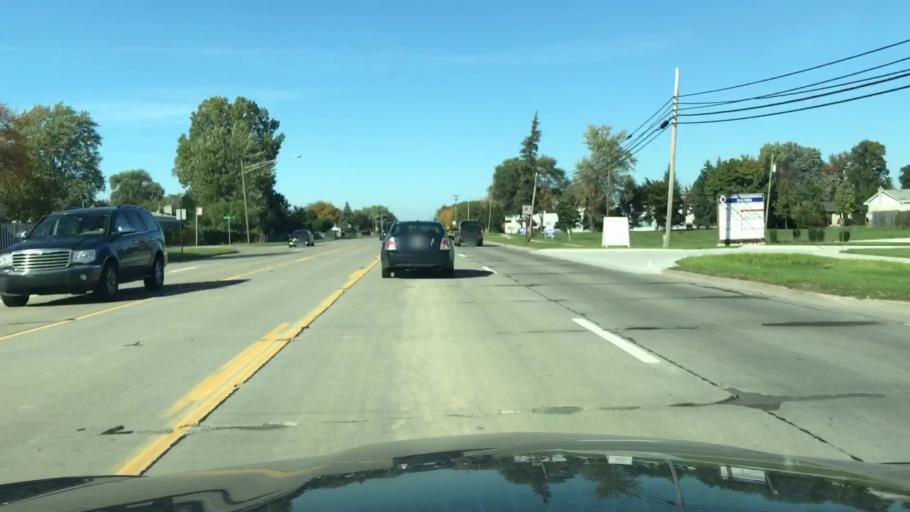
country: US
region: Michigan
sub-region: Oakland County
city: Clawson
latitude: 42.5536
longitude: -83.0883
